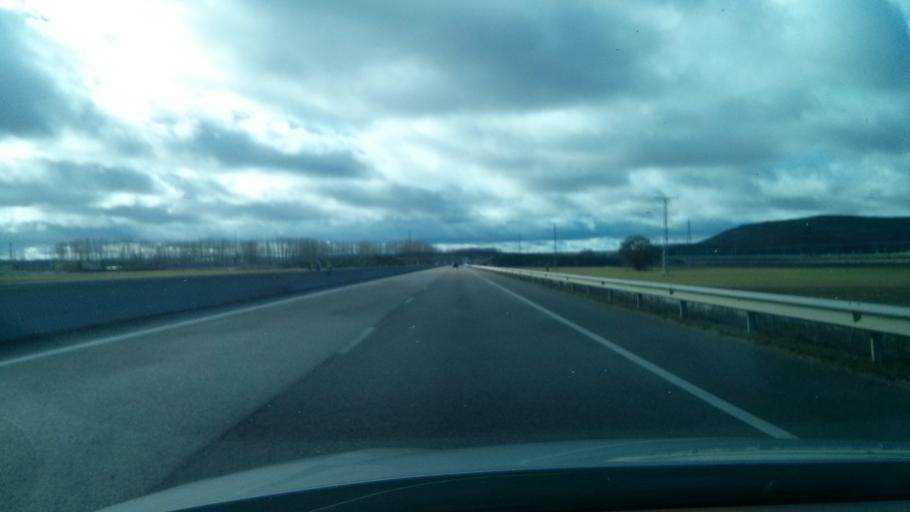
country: ES
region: Castille and Leon
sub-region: Provincia de Burgos
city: Villalbilla de Burgos
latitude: 42.3548
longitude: -3.7801
